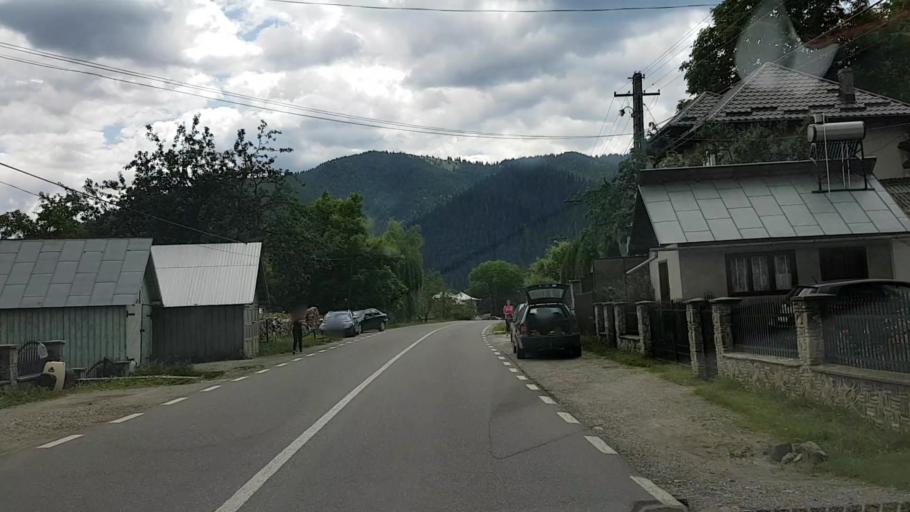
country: RO
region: Neamt
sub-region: Comuna Borca
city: Borca
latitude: 47.2121
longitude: 25.7559
